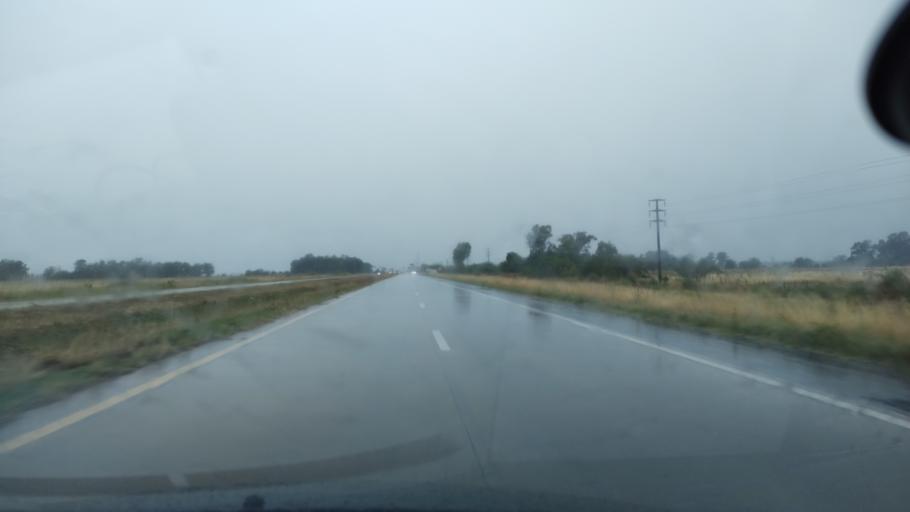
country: AR
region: Buenos Aires
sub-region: Partido de San Vicente
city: San Vicente
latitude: -35.0693
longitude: -58.5149
